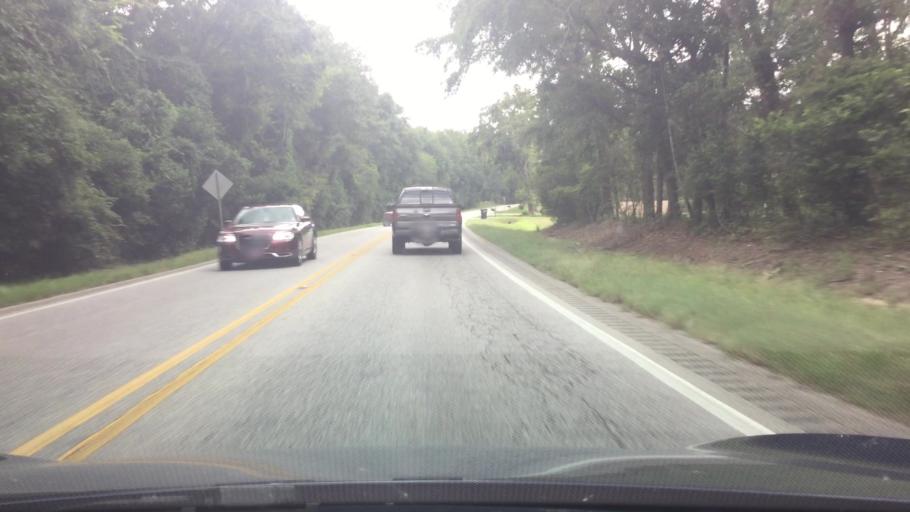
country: US
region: Alabama
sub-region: Pike County
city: Troy
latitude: 31.7520
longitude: -85.9594
